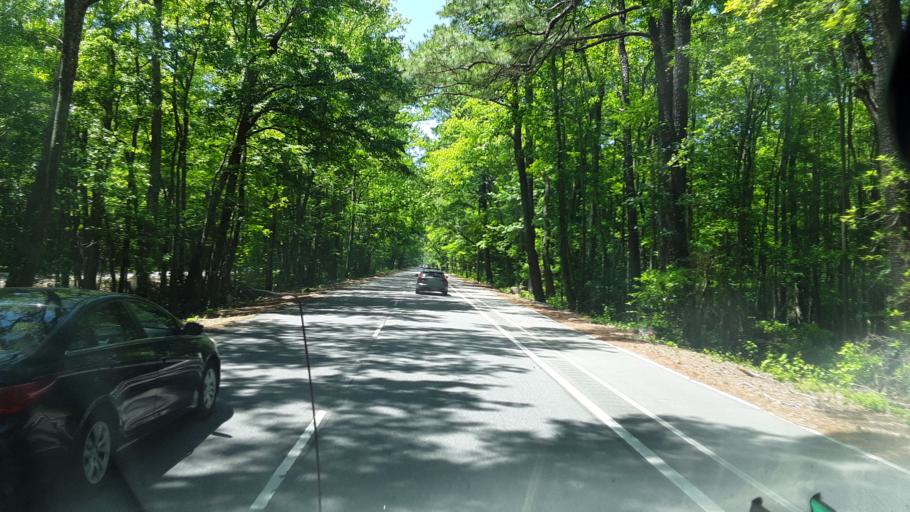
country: US
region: Virginia
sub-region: City of Virginia Beach
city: Virginia Beach
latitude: 36.9200
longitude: -76.0241
